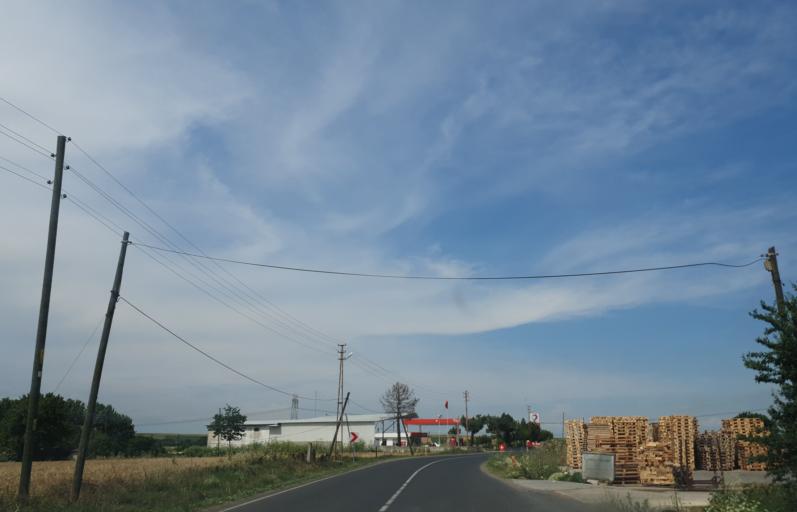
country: TR
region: Tekirdag
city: Muratli
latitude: 41.2214
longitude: 27.5486
